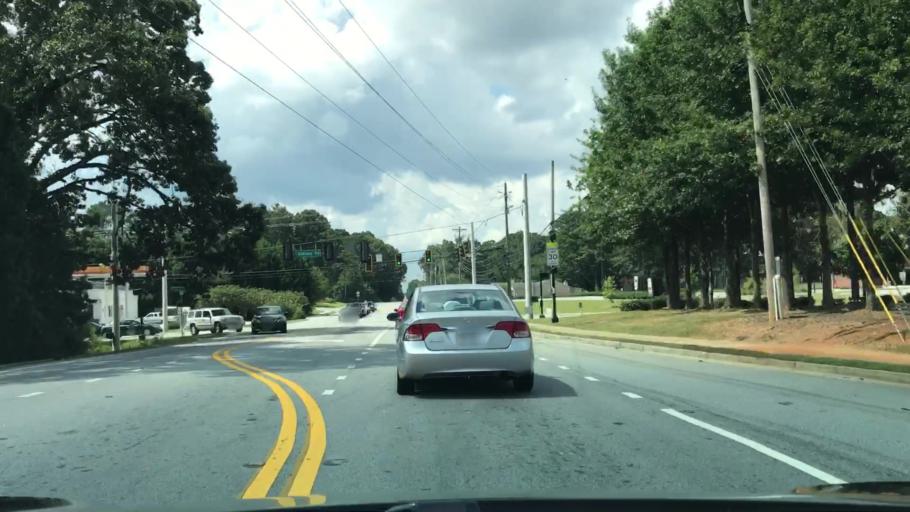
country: US
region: Georgia
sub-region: Gwinnett County
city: Lawrenceville
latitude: 33.9486
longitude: -84.0641
